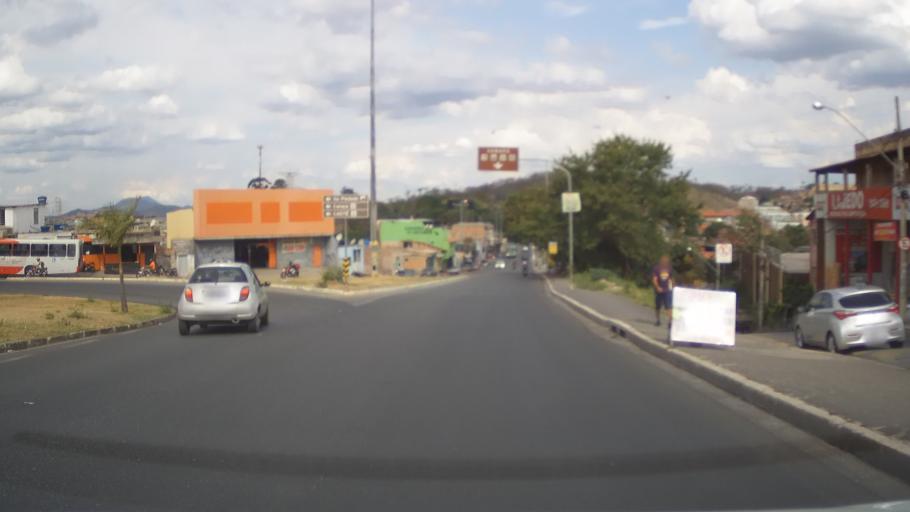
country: BR
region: Minas Gerais
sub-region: Belo Horizonte
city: Belo Horizonte
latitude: -19.8757
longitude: -43.9046
